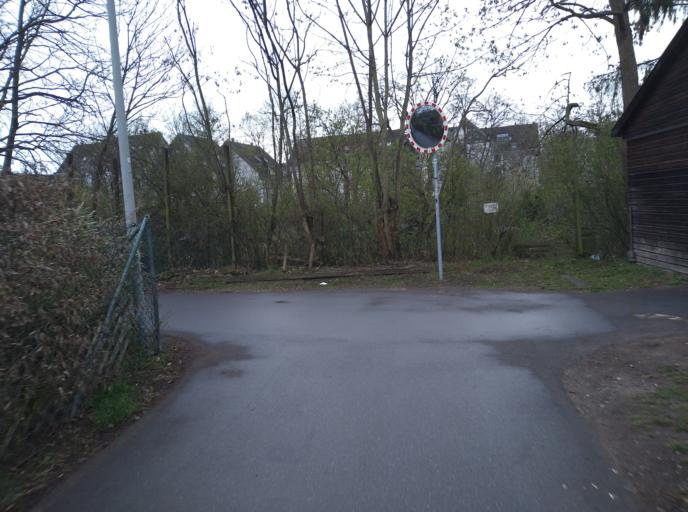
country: DE
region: Bavaria
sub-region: Regierungsbezirk Mittelfranken
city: Nuernberg
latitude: 49.4475
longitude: 11.1117
